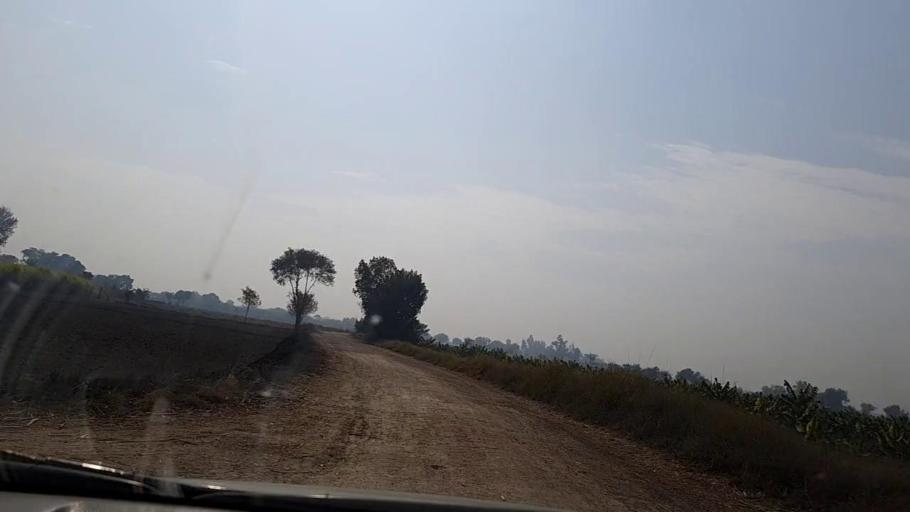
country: PK
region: Sindh
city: Daulatpur
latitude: 26.5366
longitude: 67.9867
